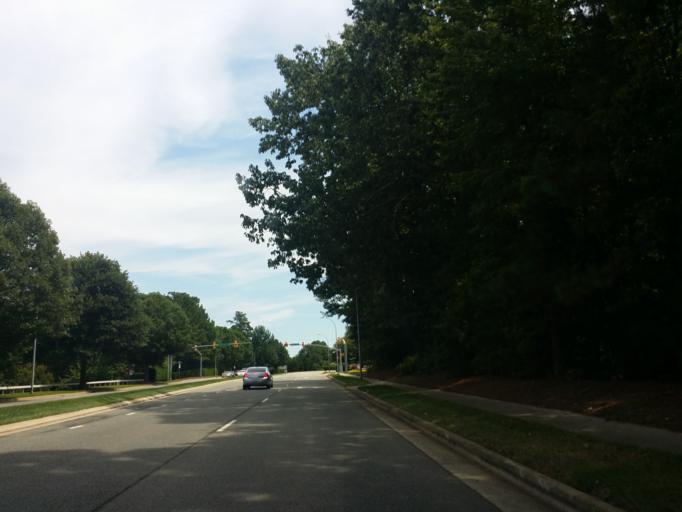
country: US
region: North Carolina
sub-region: Wake County
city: Cary
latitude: 35.8300
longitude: -78.7741
